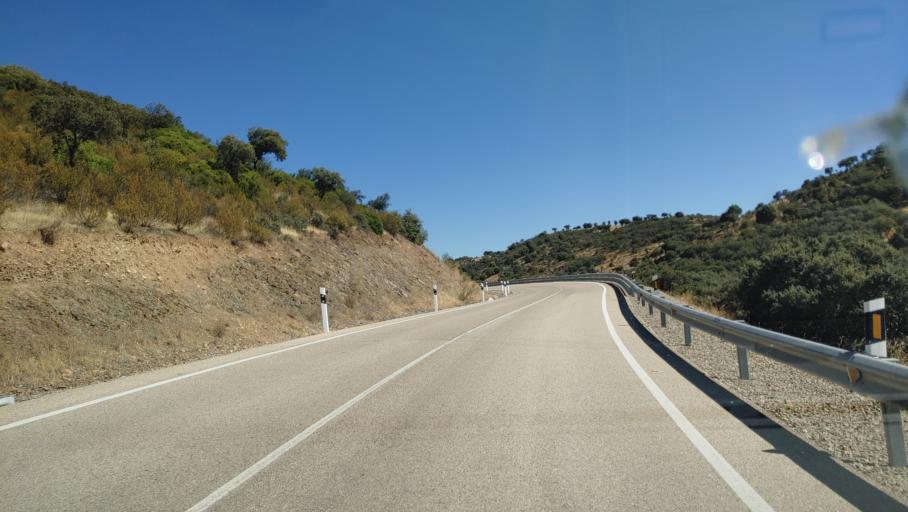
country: ES
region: Andalusia
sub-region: Provincia de Jaen
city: Genave
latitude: 38.4993
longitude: -2.7693
